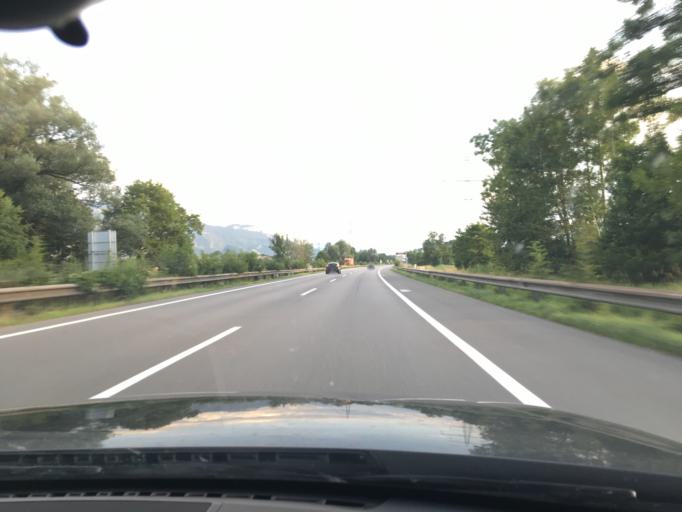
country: AT
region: Vorarlberg
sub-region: Politischer Bezirk Dornbirn
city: Dornbirn
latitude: 47.4283
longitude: 9.7185
